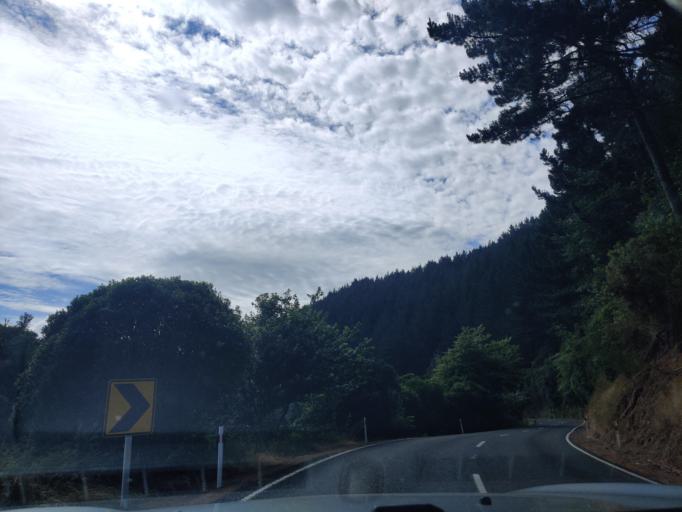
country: NZ
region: Waikato
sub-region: Otorohanga District
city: Otorohanga
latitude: -38.0969
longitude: 175.1201
